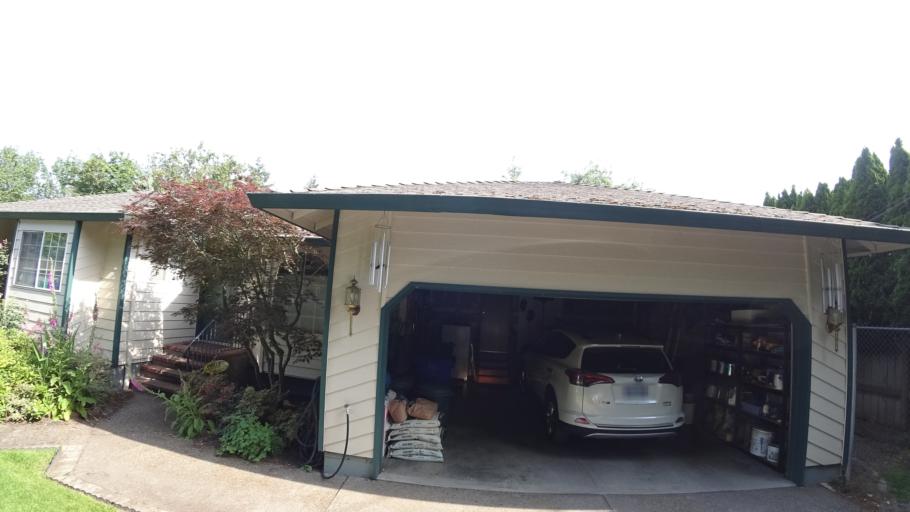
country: US
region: Oregon
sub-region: Washington County
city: Garden Home-Whitford
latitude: 45.4611
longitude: -122.7177
